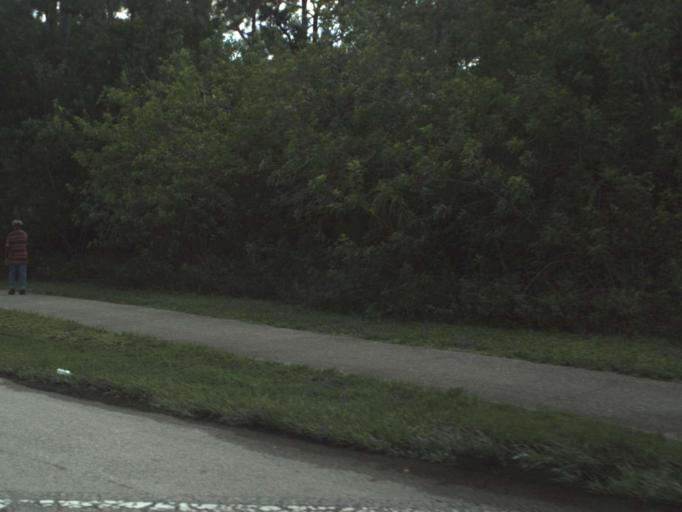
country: US
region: Florida
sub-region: Saint Lucie County
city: Port Saint Lucie
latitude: 27.2560
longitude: -80.3758
